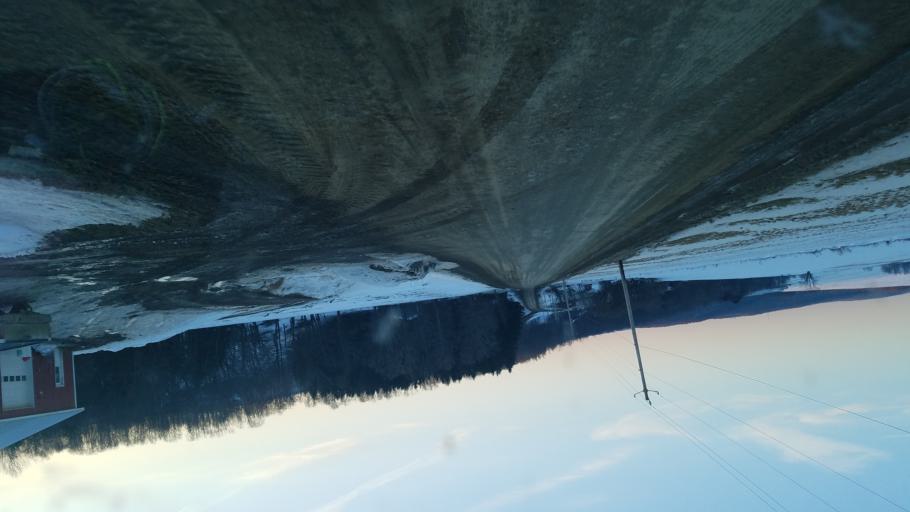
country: US
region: Pennsylvania
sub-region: Tioga County
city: Westfield
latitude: 42.0190
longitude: -77.6568
